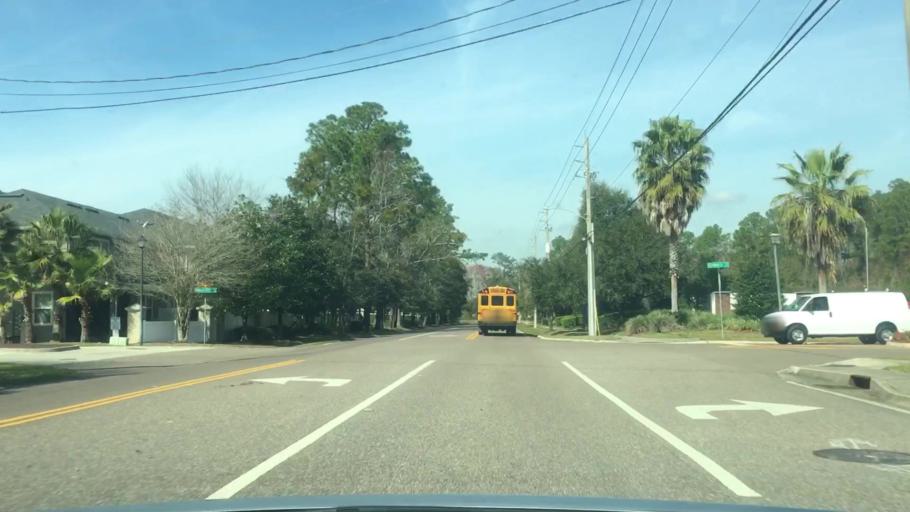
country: US
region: Florida
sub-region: Duval County
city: Jacksonville
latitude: 30.4605
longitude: -81.5606
